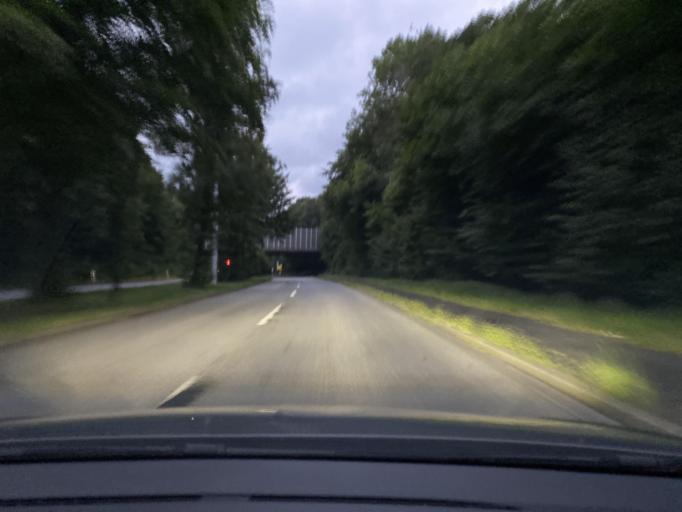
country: DE
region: North Rhine-Westphalia
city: Witten
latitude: 51.4605
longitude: 7.2989
